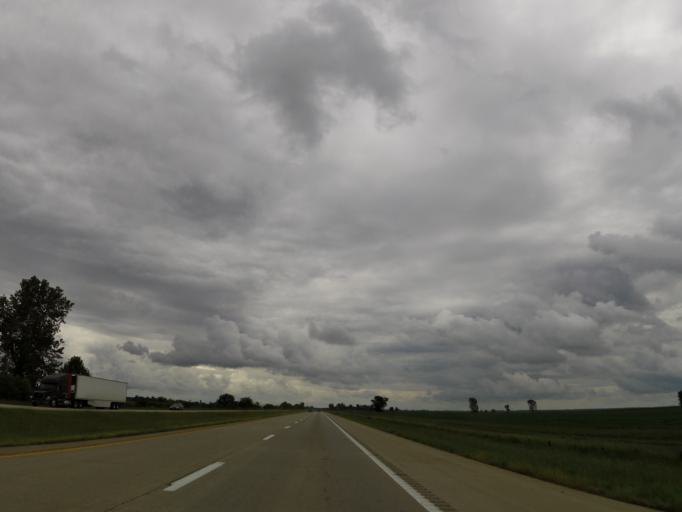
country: US
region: Missouri
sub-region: Mississippi County
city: Charleston
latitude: 36.9544
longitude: -89.2798
